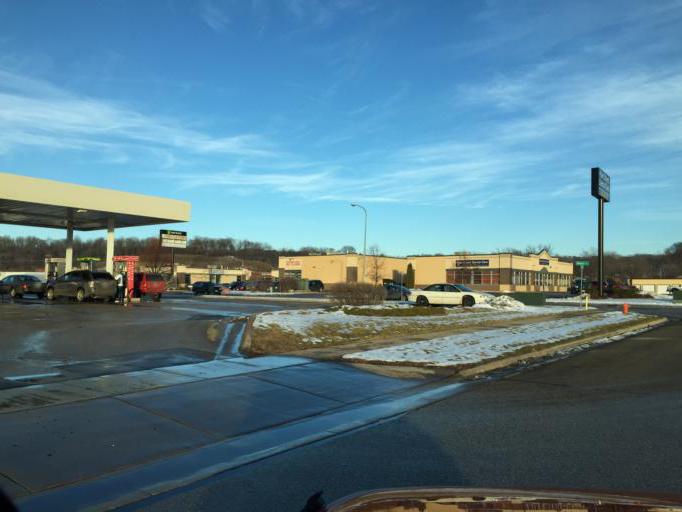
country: US
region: Minnesota
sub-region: Olmsted County
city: Rochester
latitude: 44.0559
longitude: -92.4537
